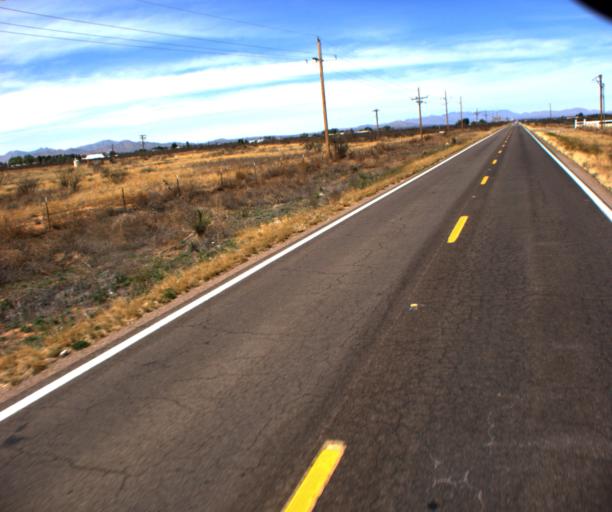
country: US
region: Arizona
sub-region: Cochise County
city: Willcox
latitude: 31.9966
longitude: -109.8592
